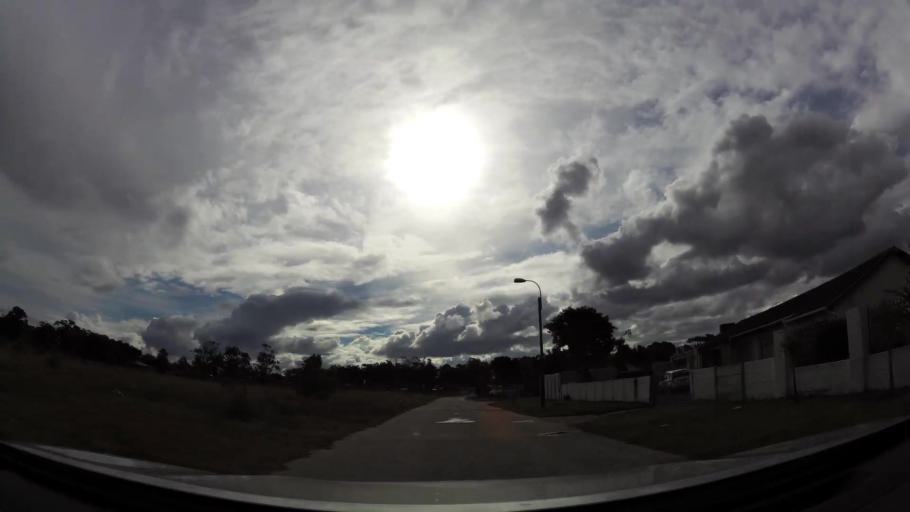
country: ZA
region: Eastern Cape
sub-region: Nelson Mandela Bay Metropolitan Municipality
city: Port Elizabeth
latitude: -33.9362
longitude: 25.4951
